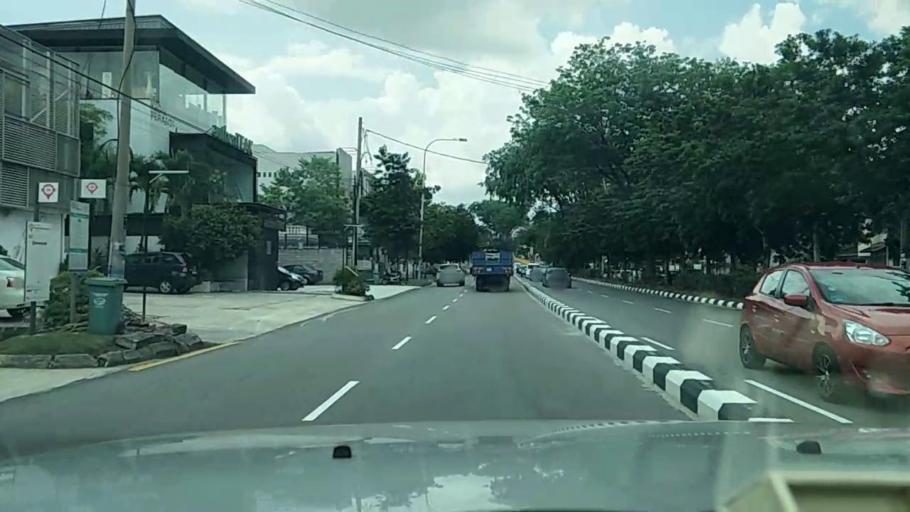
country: MY
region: Kuala Lumpur
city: Kuala Lumpur
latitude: 3.1391
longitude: 101.6723
